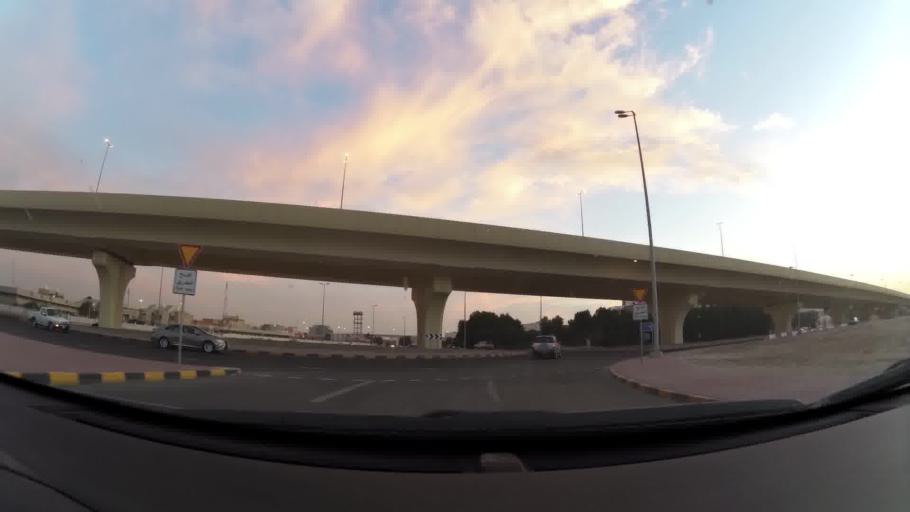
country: KW
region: Al Asimah
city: Ar Rabiyah
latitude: 29.3182
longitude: 47.8813
